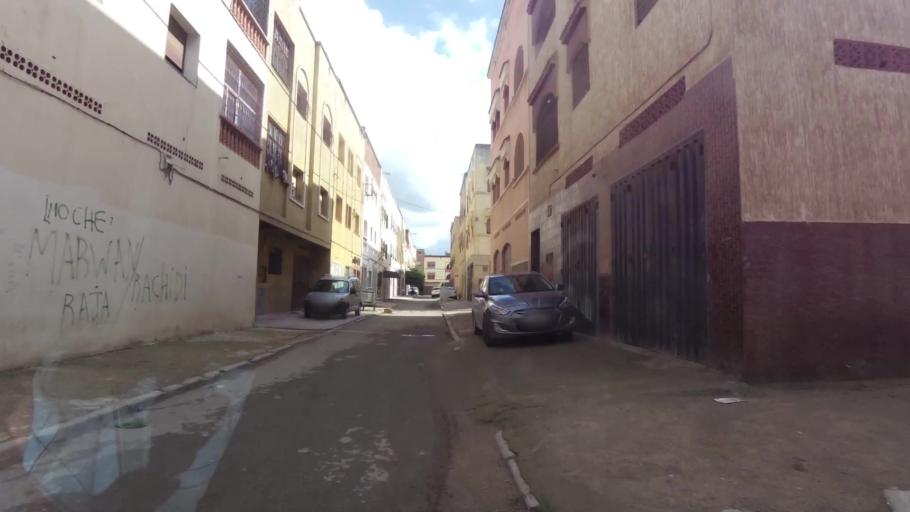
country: MA
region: Chaouia-Ouardigha
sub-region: Settat Province
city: Berrechid
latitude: 33.2654
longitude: -7.5720
